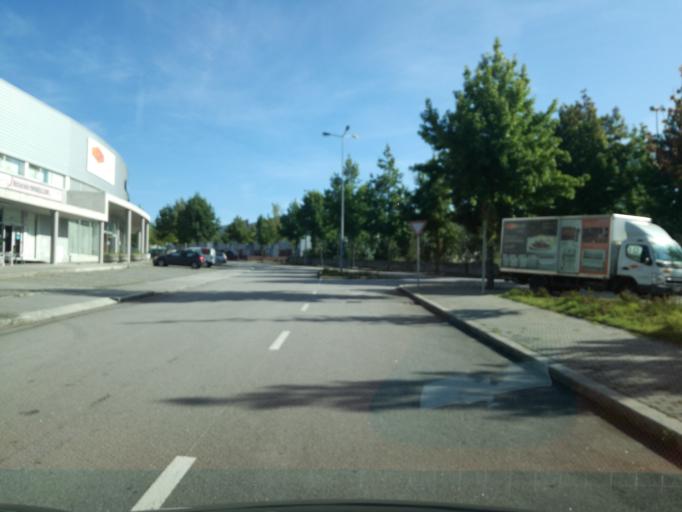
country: PT
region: Porto
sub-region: Maia
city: Anta
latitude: 41.2742
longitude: -8.6049
